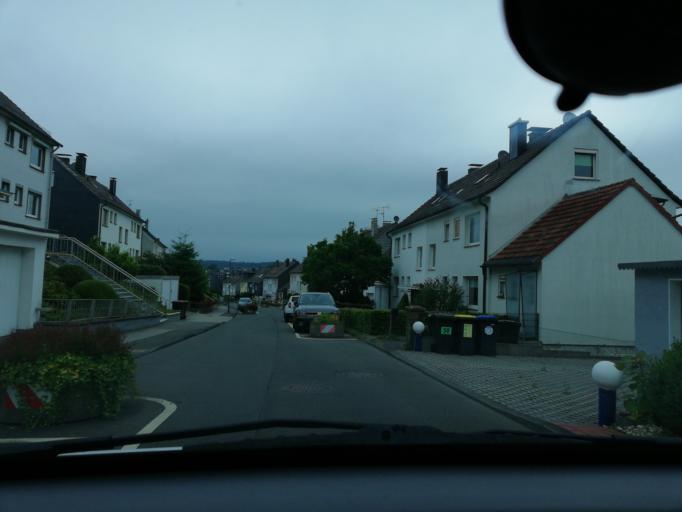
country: DE
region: North Rhine-Westphalia
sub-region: Regierungsbezirk Dusseldorf
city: Wuppertal
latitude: 51.2647
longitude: 7.2321
